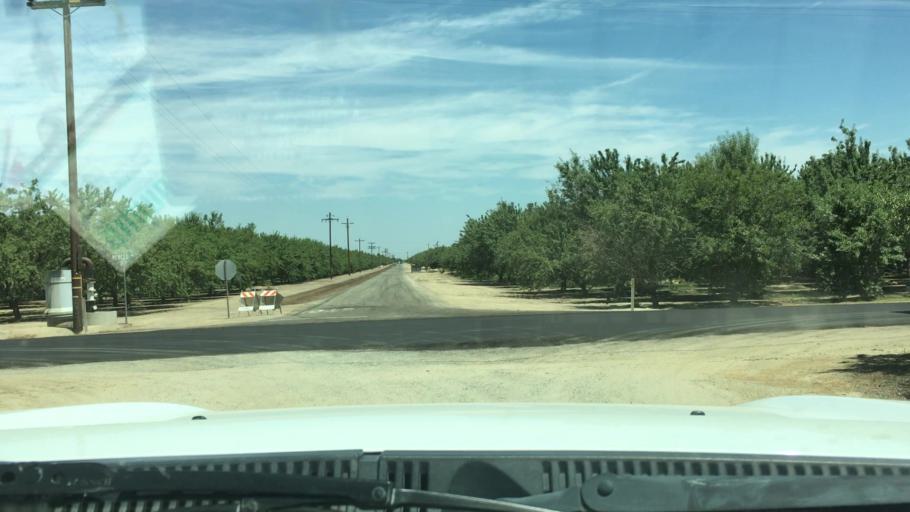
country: US
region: California
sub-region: Kern County
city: Wasco
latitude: 35.5288
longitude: -119.3410
